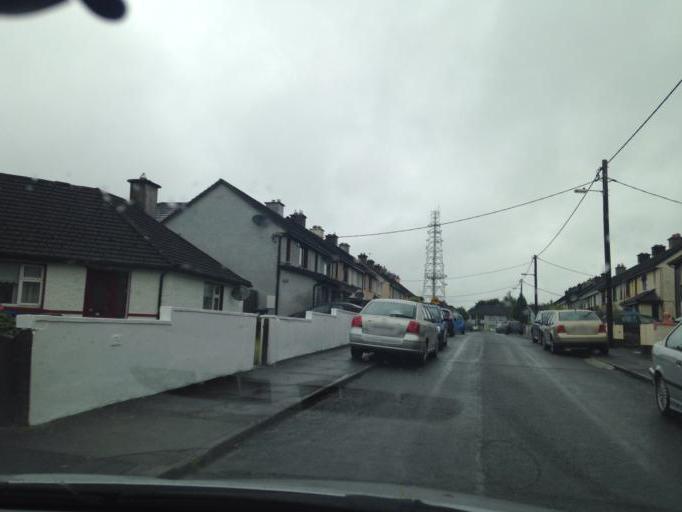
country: IE
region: Connaught
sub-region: County Galway
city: Gaillimh
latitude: 53.2859
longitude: -9.0145
